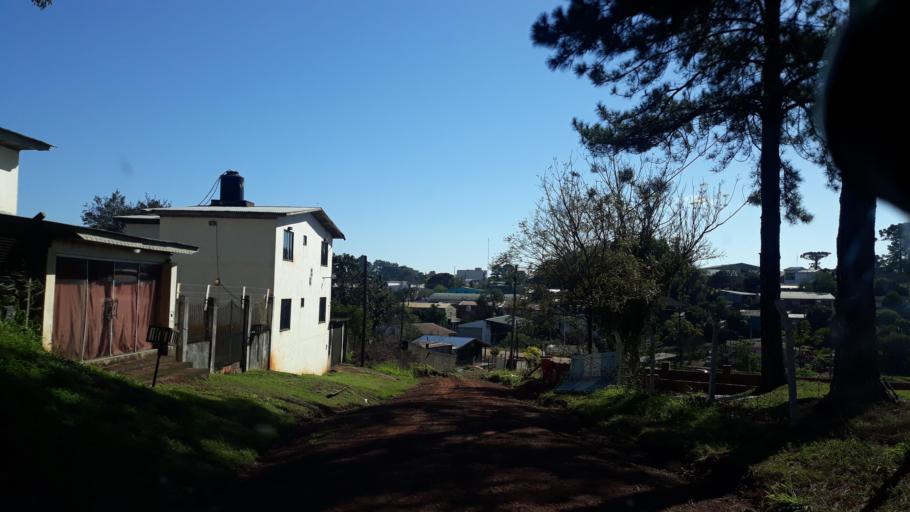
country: AR
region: Misiones
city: Bernardo de Irigoyen
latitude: -26.2612
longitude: -53.6466
